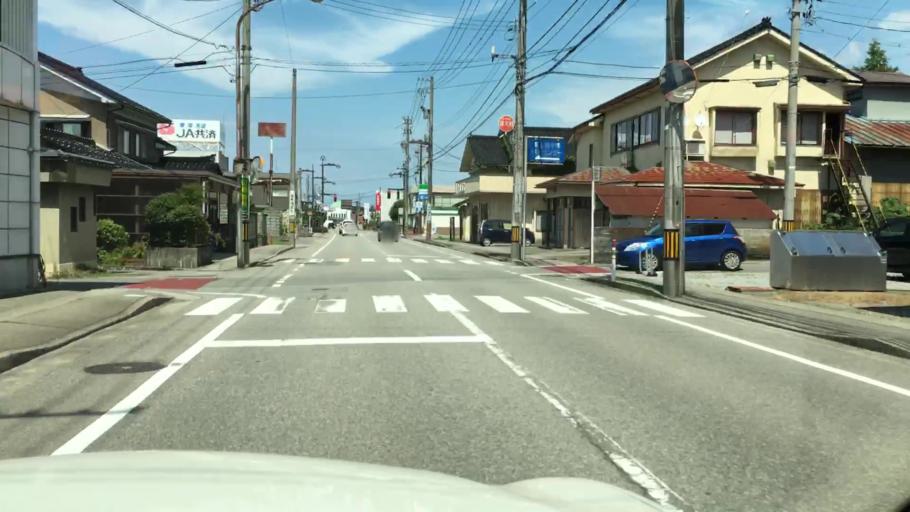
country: JP
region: Toyama
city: Kamiichi
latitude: 36.7030
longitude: 137.3580
